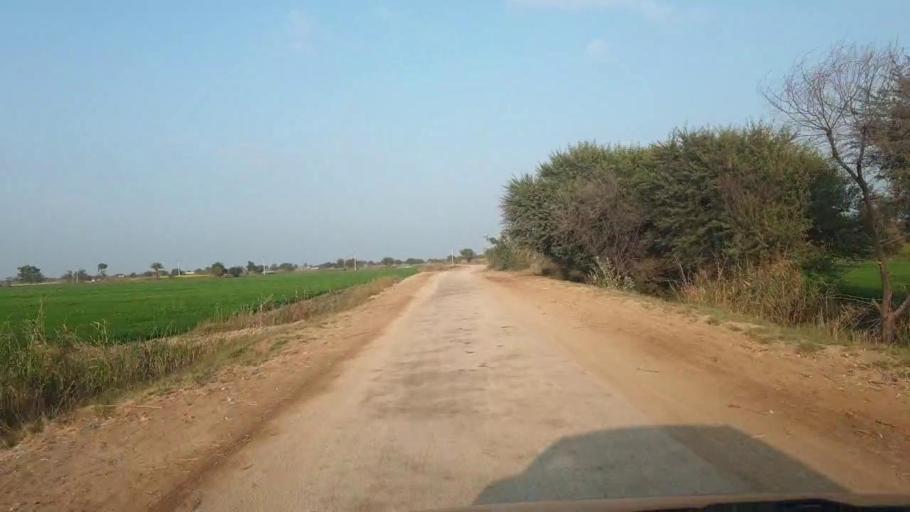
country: PK
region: Sindh
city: Berani
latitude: 25.8561
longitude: 68.7352
